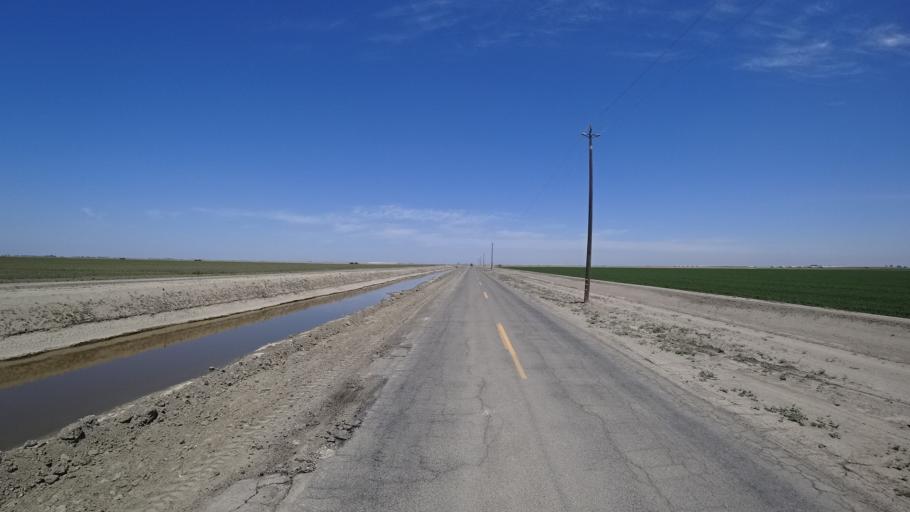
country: US
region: California
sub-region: Kings County
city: Corcoran
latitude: 36.1188
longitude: -119.6801
